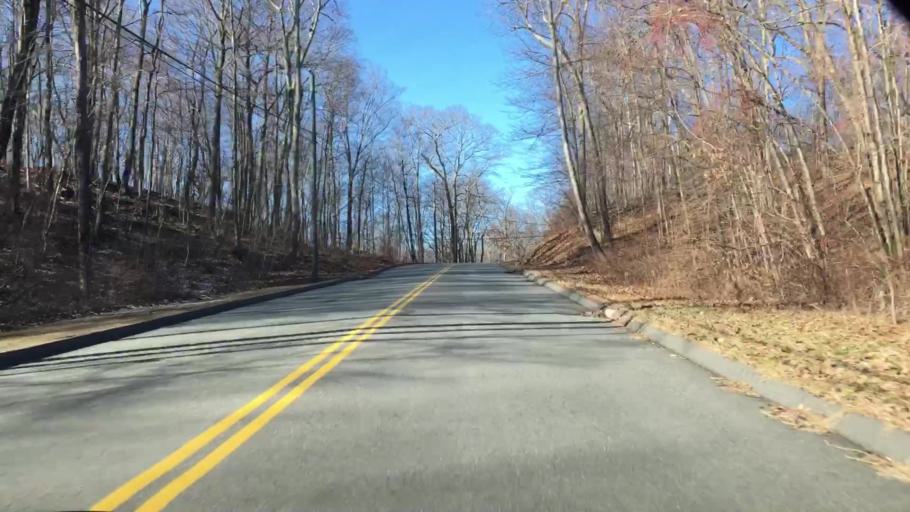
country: US
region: Connecticut
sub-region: Tolland County
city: Tolland
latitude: 41.8836
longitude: -72.3857
